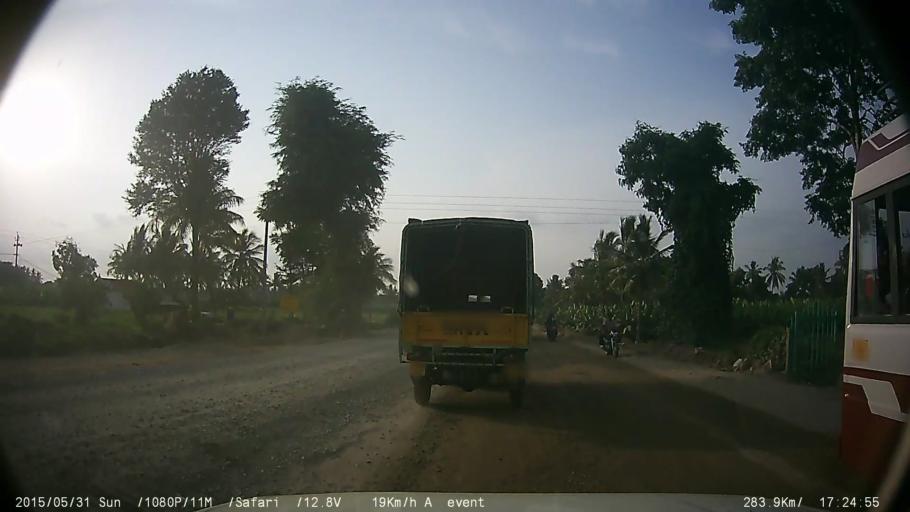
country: IN
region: Karnataka
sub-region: Chamrajnagar
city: Gundlupet
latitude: 11.8504
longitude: 76.6718
